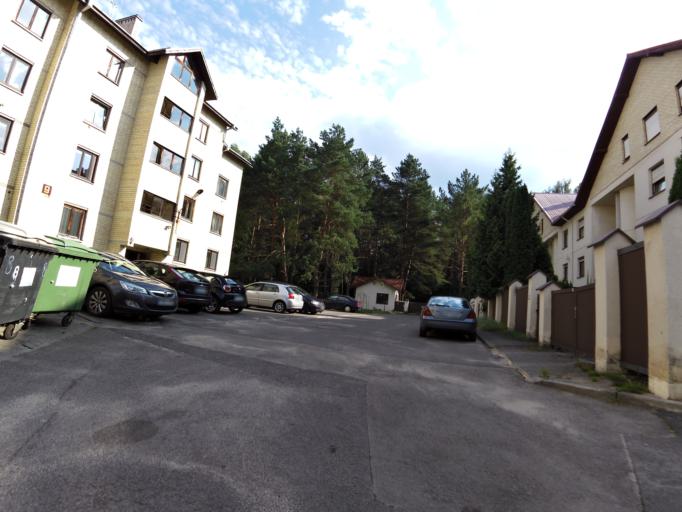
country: LT
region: Vilnius County
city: Lazdynai
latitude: 54.6650
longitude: 25.2167
